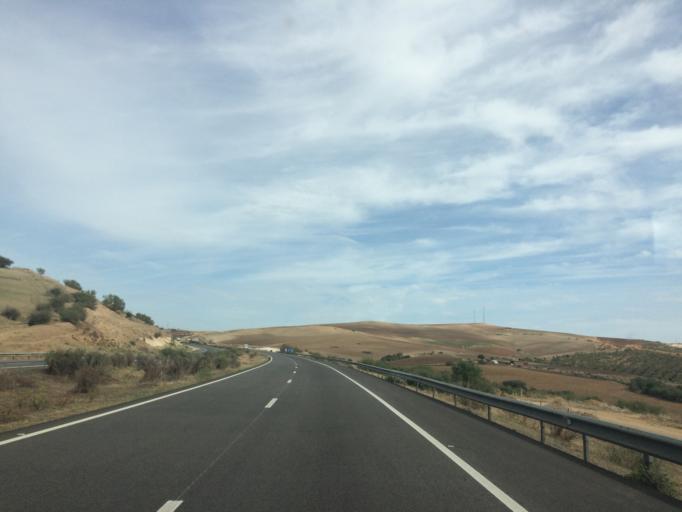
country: MA
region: Meknes-Tafilalet
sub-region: Meknes
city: Meknes
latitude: 33.8610
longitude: -5.7878
